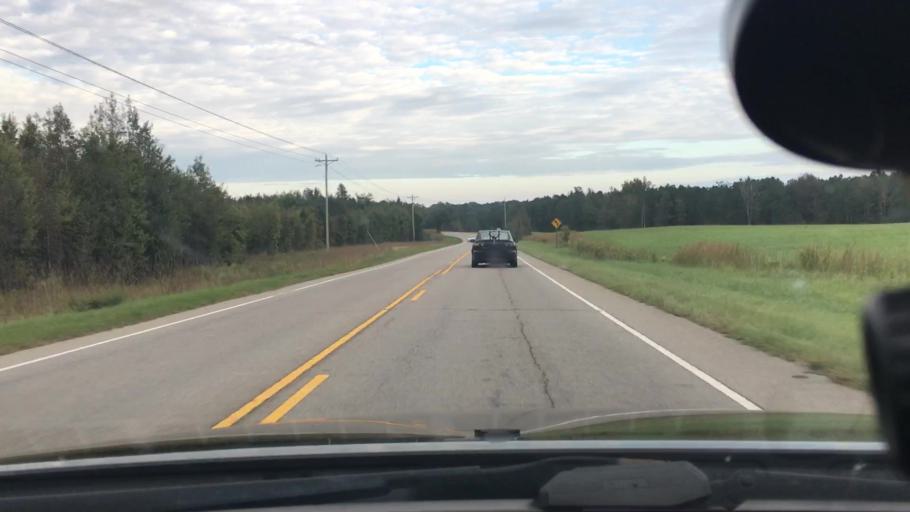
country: US
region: North Carolina
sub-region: Moore County
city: Robbins
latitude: 35.3998
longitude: -79.5508
